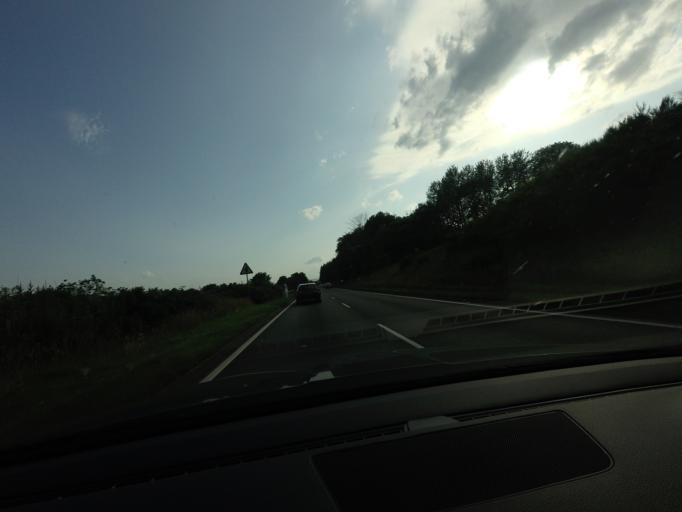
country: GB
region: Scotland
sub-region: Highland
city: Evanton
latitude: 57.6429
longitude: -4.3458
